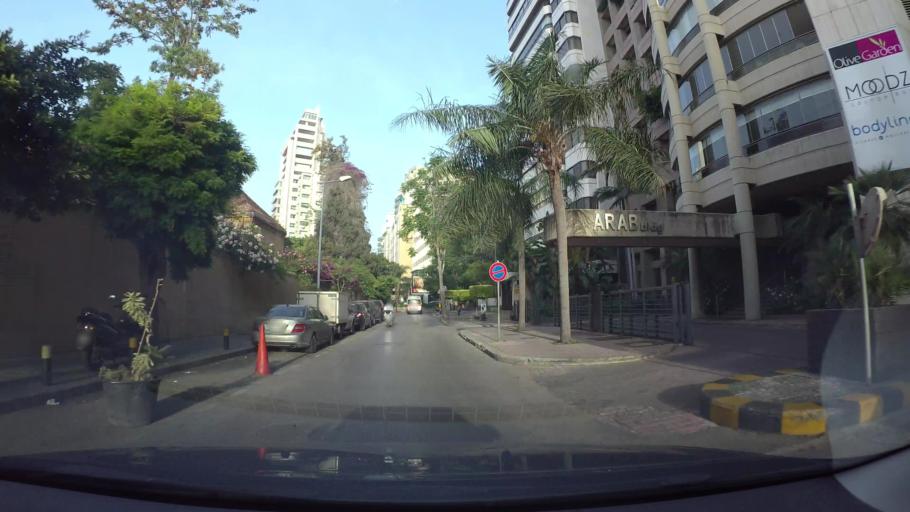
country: LB
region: Beyrouth
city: Ra's Bayrut
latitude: 33.8983
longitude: 35.4879
